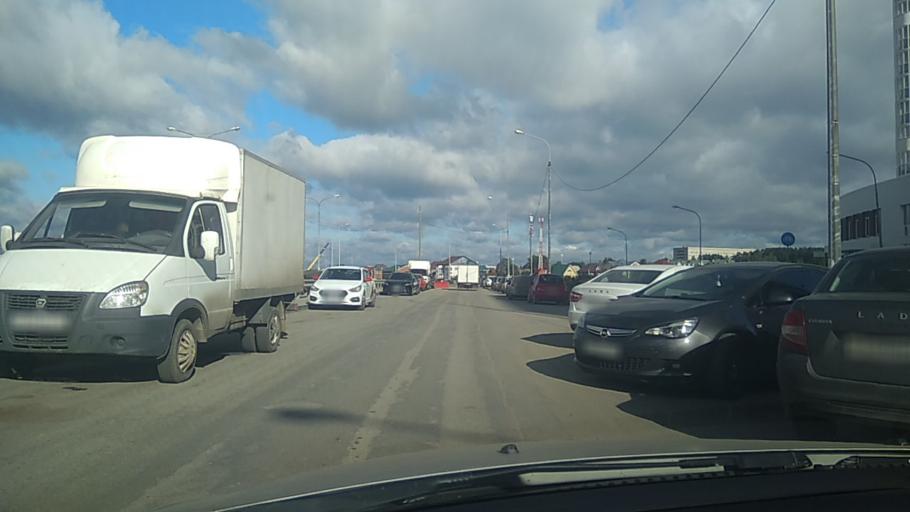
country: RU
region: Sverdlovsk
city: Shirokaya Rechka
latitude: 56.7985
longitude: 60.5121
